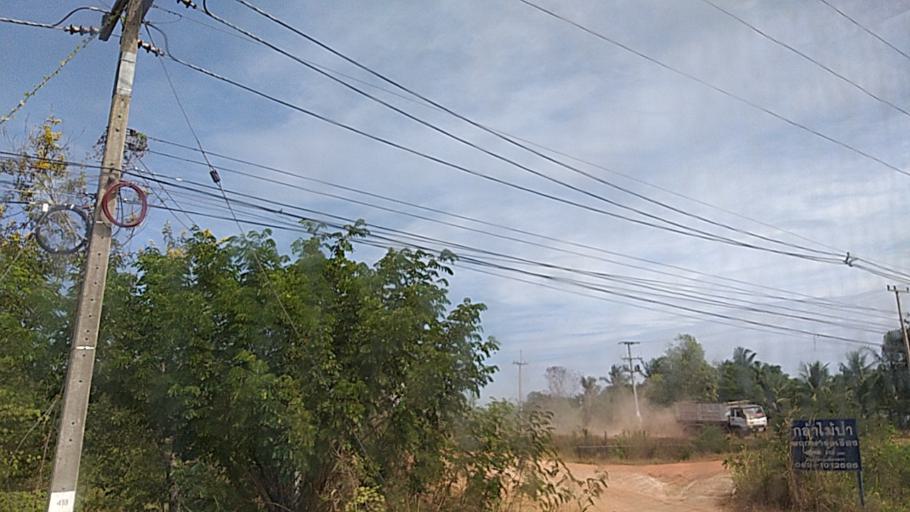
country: TH
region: Maha Sarakham
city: Chiang Yuen
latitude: 16.4430
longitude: 102.9914
